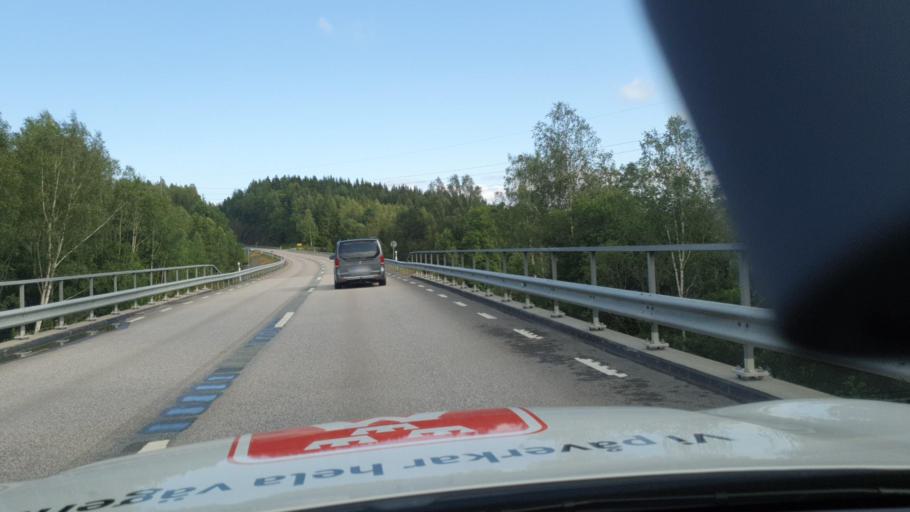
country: SE
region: Vaestra Goetaland
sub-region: Bengtsfors Kommun
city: Billingsfors
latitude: 58.9295
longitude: 12.1351
